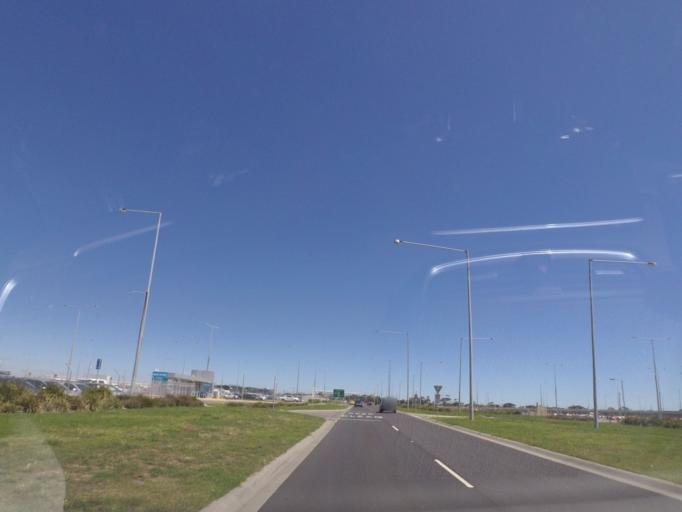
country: AU
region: Victoria
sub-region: Hume
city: Westmeadows
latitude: -37.6807
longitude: 144.8617
